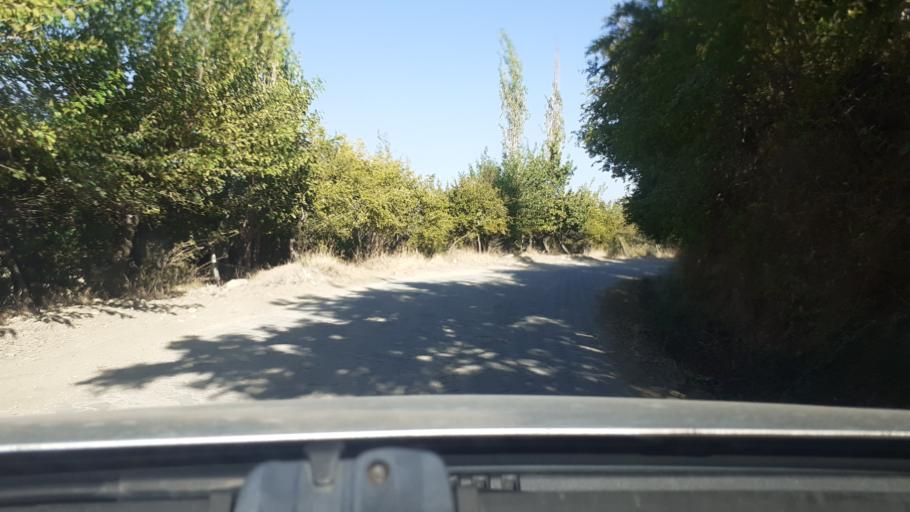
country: TR
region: Hatay
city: Kirikhan
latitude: 36.4889
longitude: 36.2991
